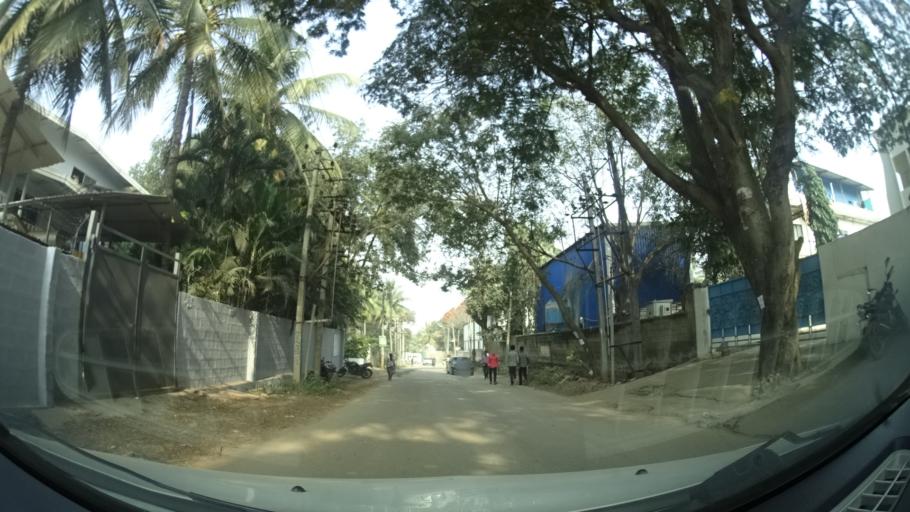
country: IN
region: Karnataka
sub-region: Bangalore Urban
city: Anekal
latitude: 12.8193
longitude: 77.6741
